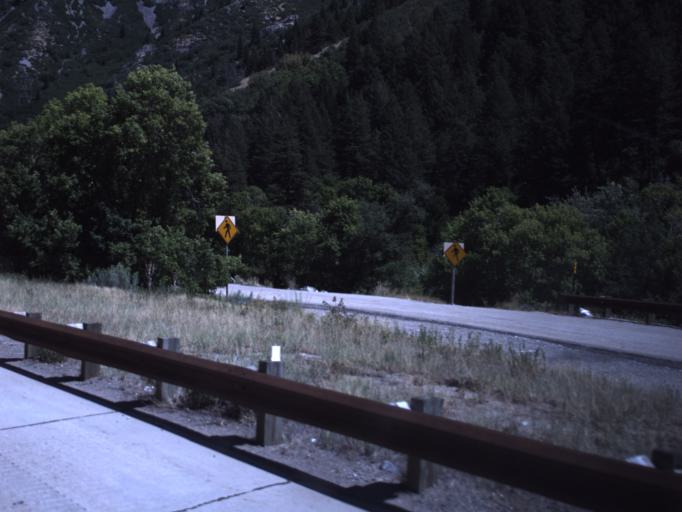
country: US
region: Utah
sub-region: Utah County
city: Orem
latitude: 40.3620
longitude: -111.5616
